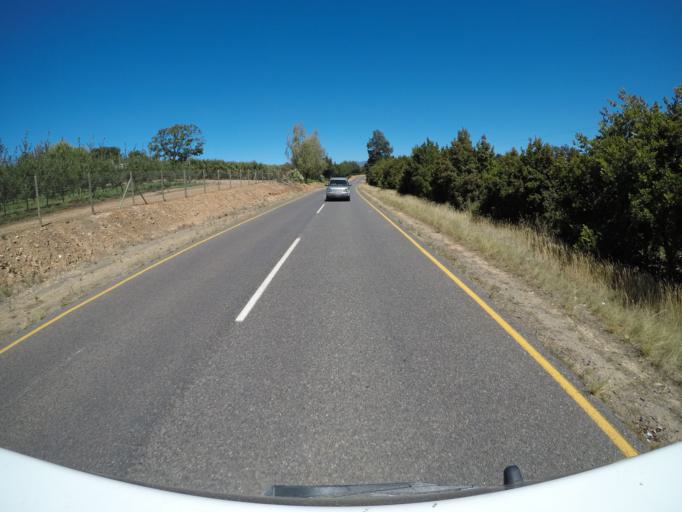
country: ZA
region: Western Cape
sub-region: Overberg District Municipality
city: Grabouw
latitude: -34.2108
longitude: 19.0482
